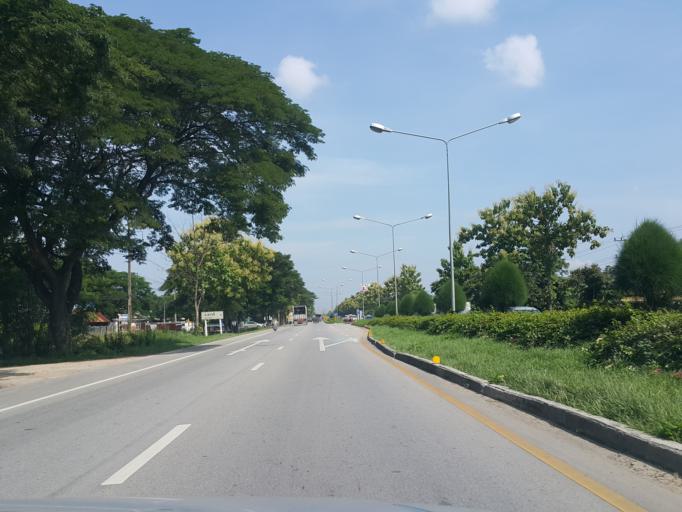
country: TH
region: Chiang Mai
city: Saraphi
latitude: 18.7118
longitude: 99.0447
